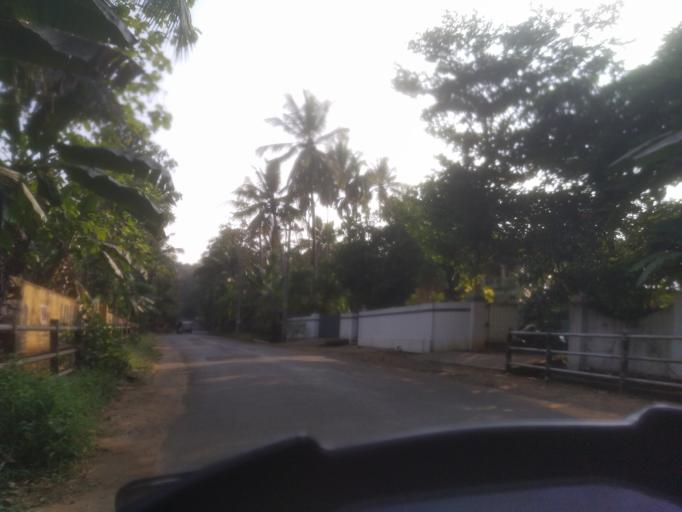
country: IN
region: Kerala
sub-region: Ernakulam
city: Piravam
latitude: 9.8148
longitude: 76.4992
